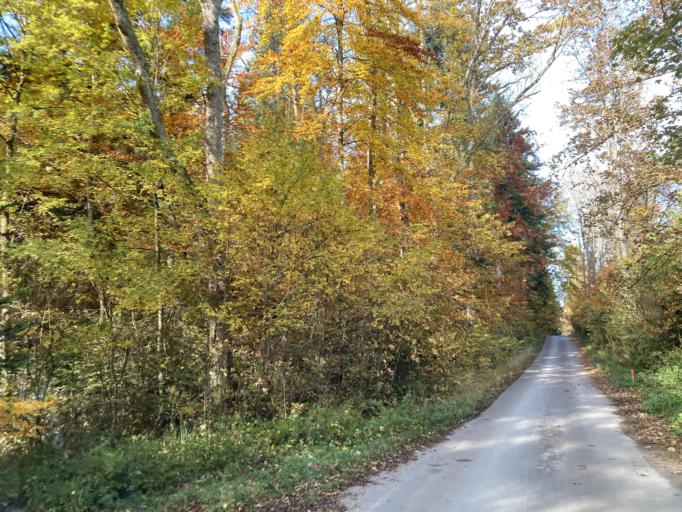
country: DE
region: Baden-Wuerttemberg
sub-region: Tuebingen Region
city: Rottenburg
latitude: 48.4526
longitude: 8.9460
